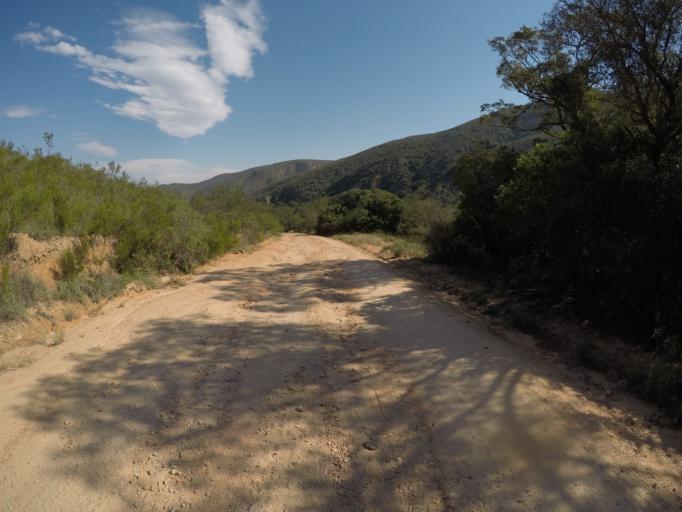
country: ZA
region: Eastern Cape
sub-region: Cacadu District Municipality
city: Kareedouw
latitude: -33.6448
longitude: 24.4596
